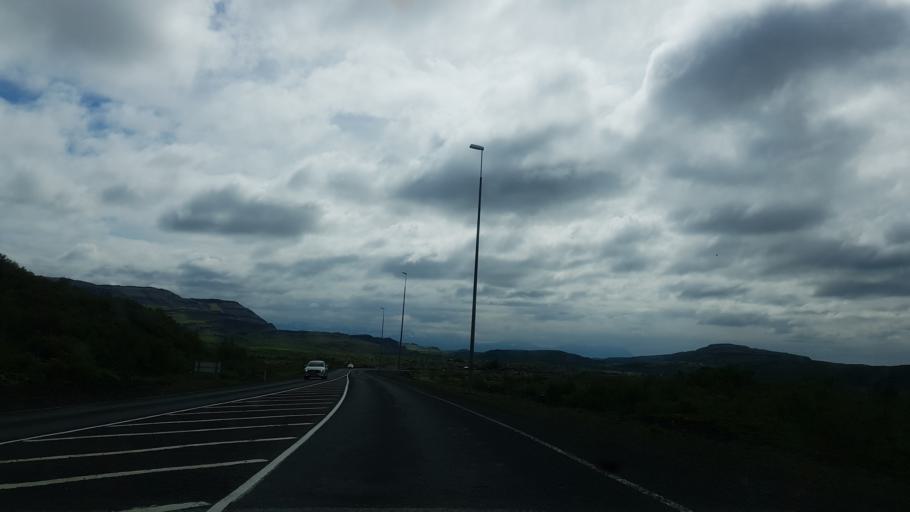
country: IS
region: West
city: Borgarnes
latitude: 64.7630
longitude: -21.5539
